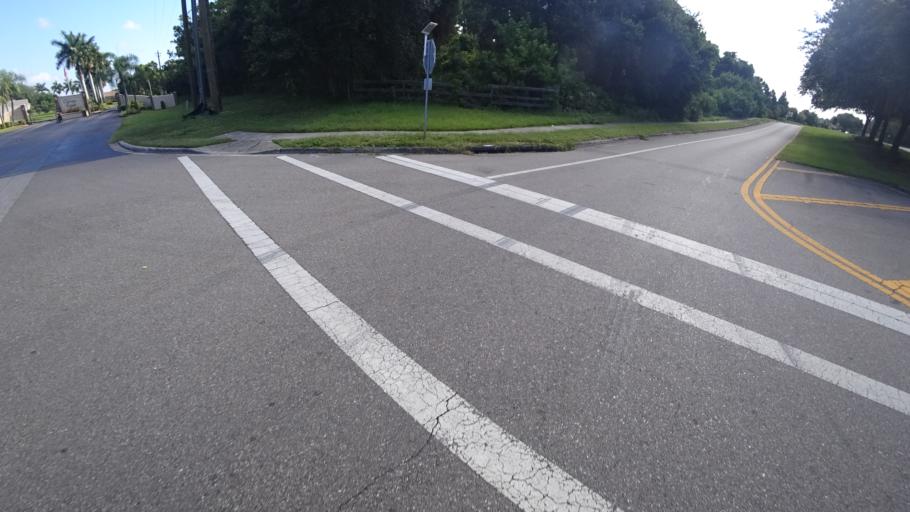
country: US
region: Florida
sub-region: Manatee County
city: Ellenton
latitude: 27.5063
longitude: -82.4814
